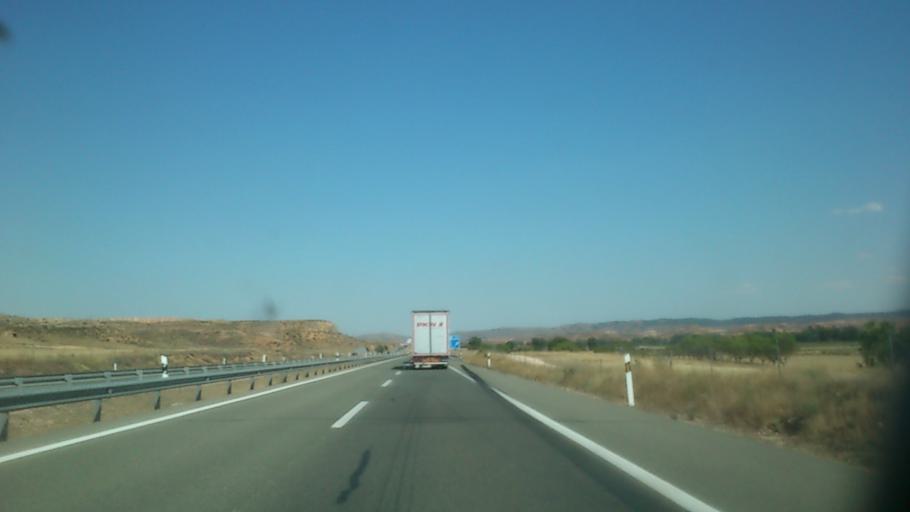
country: ES
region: Aragon
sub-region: Provincia de Zaragoza
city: Cetina
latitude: 41.3071
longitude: -1.9878
